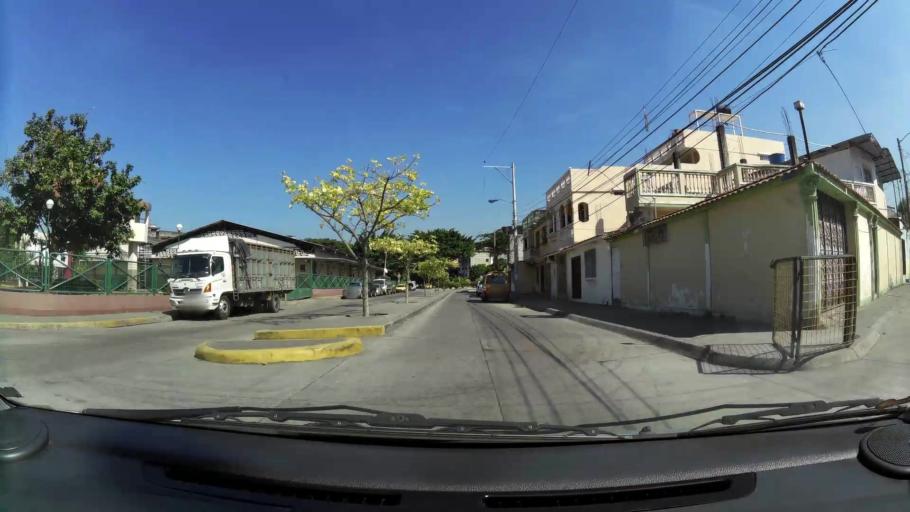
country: EC
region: Guayas
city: Eloy Alfaro
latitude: -2.1240
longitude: -79.8844
